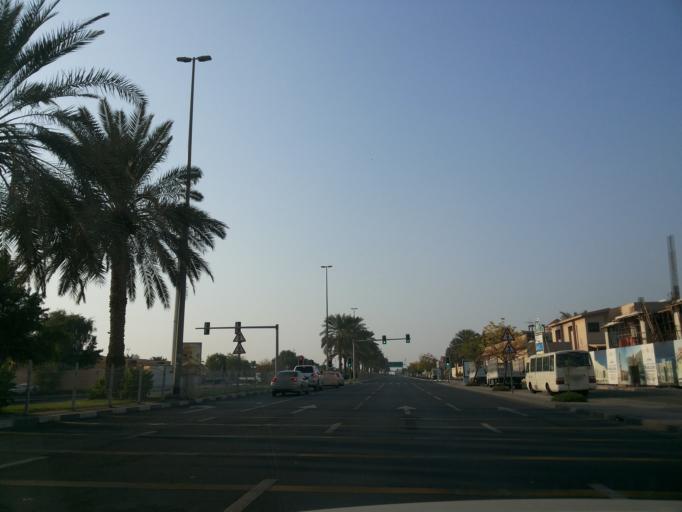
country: AE
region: Ash Shariqah
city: Sharjah
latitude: 25.2946
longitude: 55.3404
